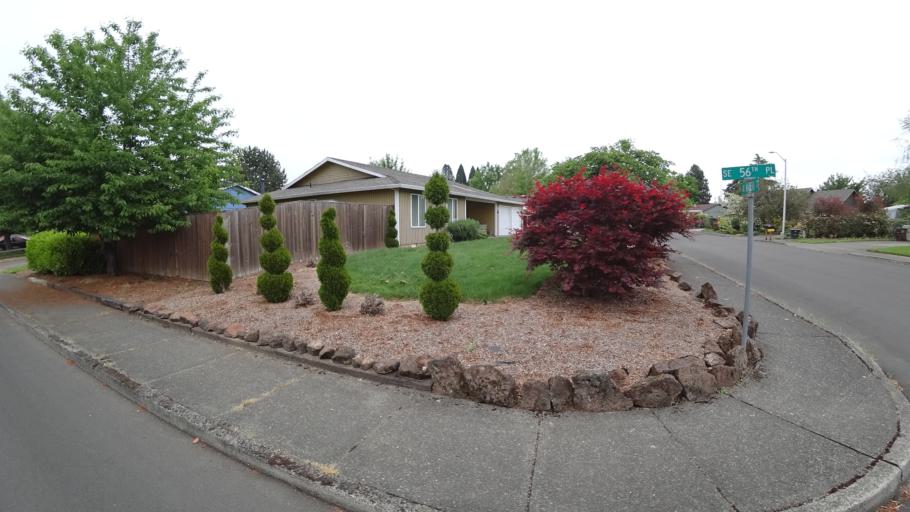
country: US
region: Oregon
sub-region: Washington County
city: Aloha
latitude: 45.5019
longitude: -122.9247
